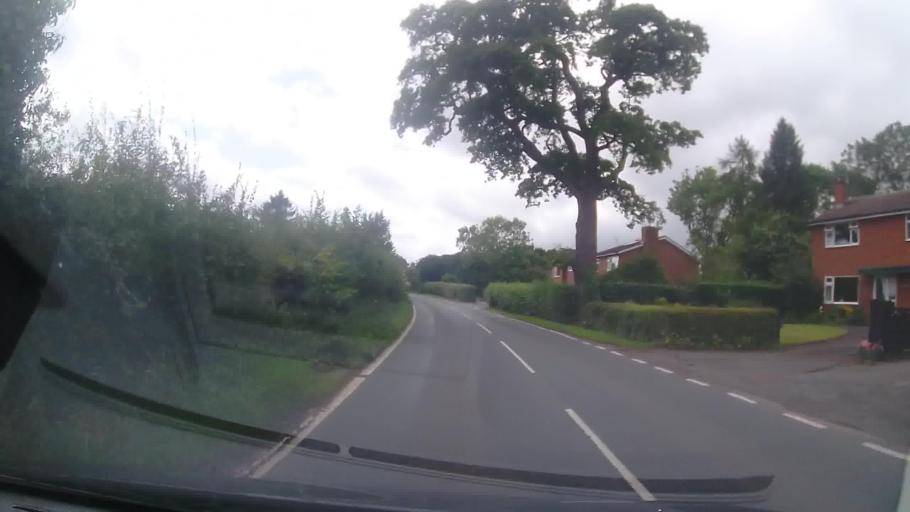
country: GB
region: England
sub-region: Shropshire
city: Craven Arms
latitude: 52.4360
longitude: -2.8674
